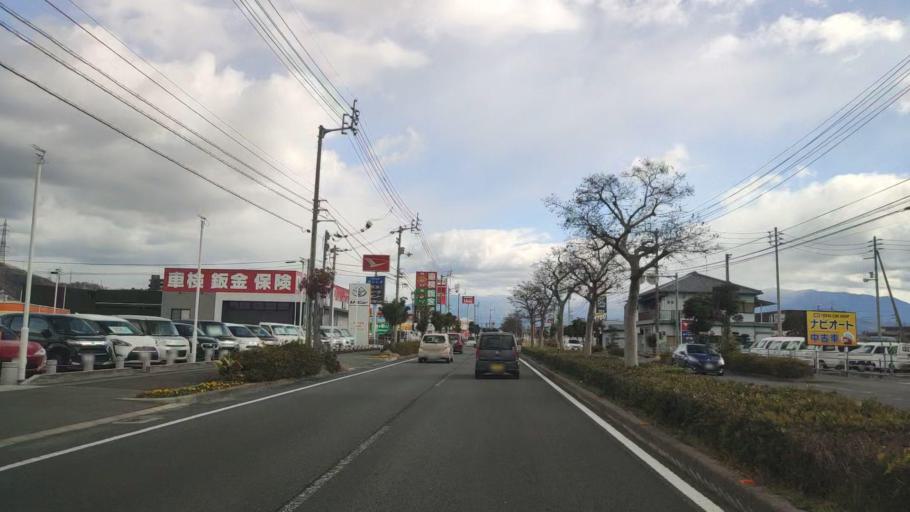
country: JP
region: Ehime
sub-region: Shikoku-chuo Shi
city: Matsuyama
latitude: 33.8198
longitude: 132.7898
